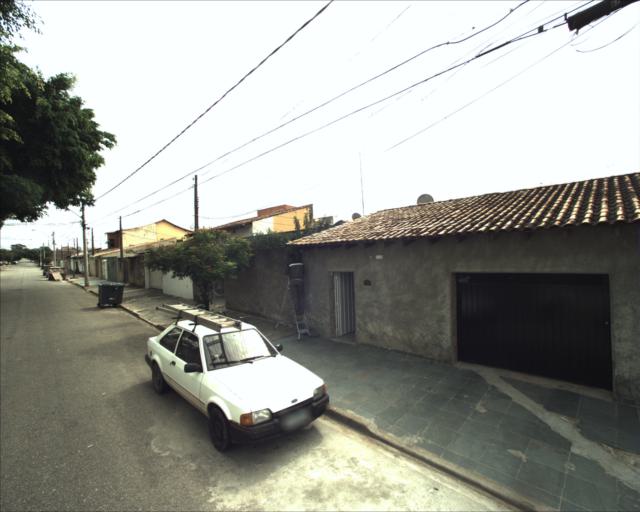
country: BR
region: Sao Paulo
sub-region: Sorocaba
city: Sorocaba
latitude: -23.5075
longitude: -47.5120
